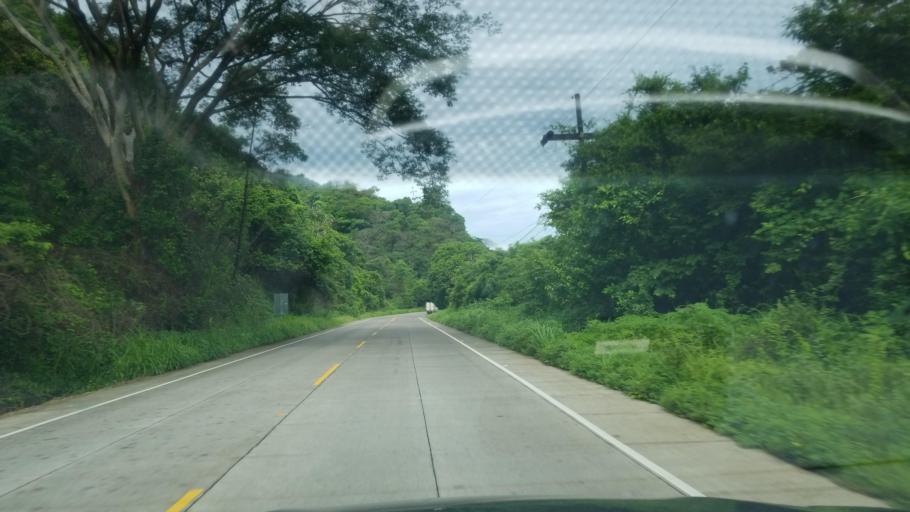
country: HN
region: Francisco Morazan
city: El Porvenir
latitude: 13.6861
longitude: -87.3453
